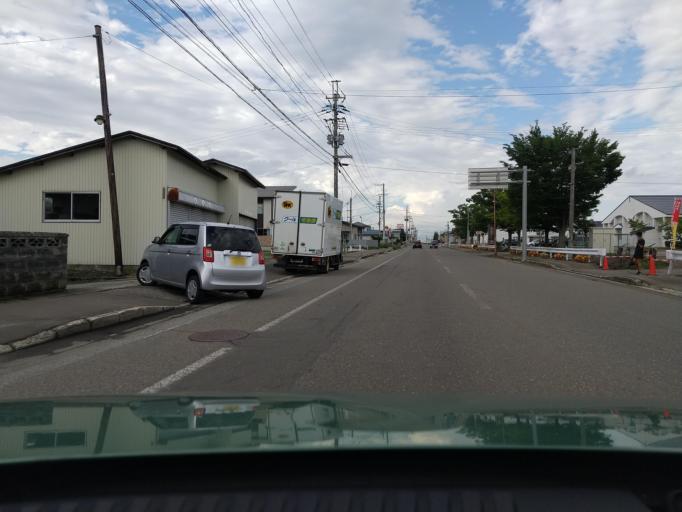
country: JP
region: Akita
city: Yokotemachi
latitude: 39.2622
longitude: 140.4908
